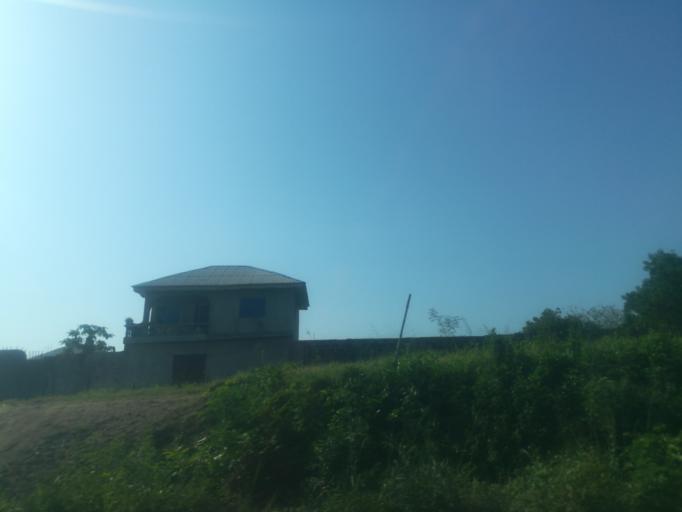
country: NG
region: Ogun
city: Abeokuta
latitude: 7.1614
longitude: 3.2665
